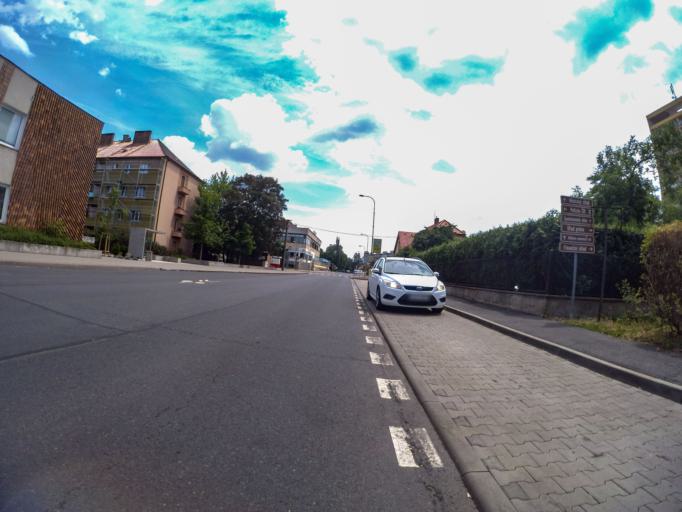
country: CZ
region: Central Bohemia
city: Neratovice
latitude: 50.2598
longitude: 14.5169
